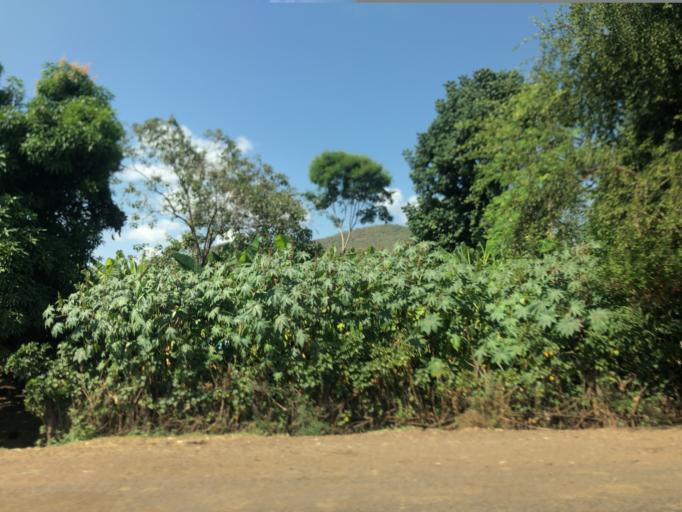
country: ET
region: Southern Nations, Nationalities, and People's Region
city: Gidole
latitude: 5.8293
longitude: 37.4554
